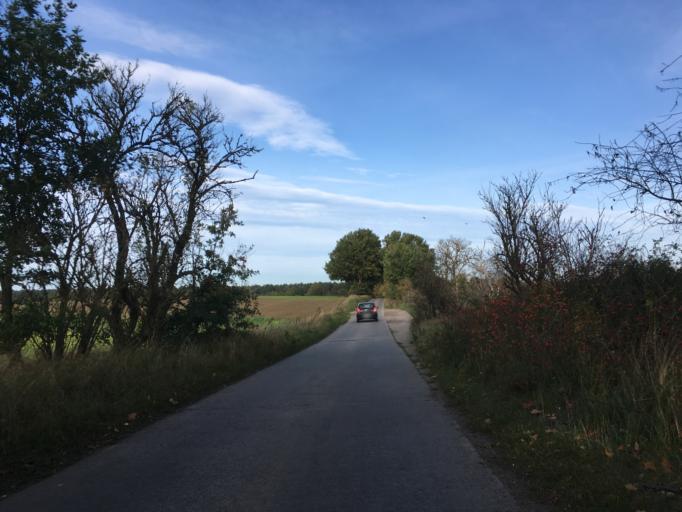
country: DE
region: Brandenburg
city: Wandlitz
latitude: 52.7417
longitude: 13.4364
